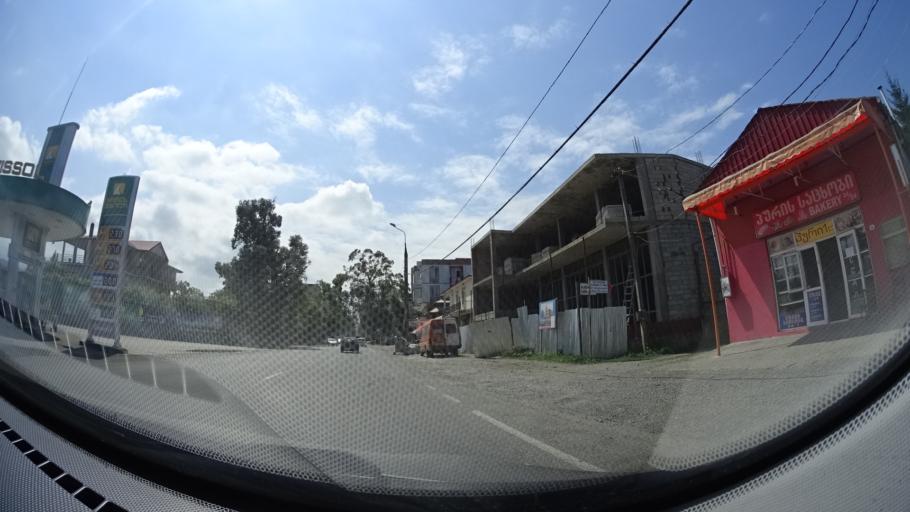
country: GE
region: Ajaria
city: Batumi
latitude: 41.6169
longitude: 41.6196
